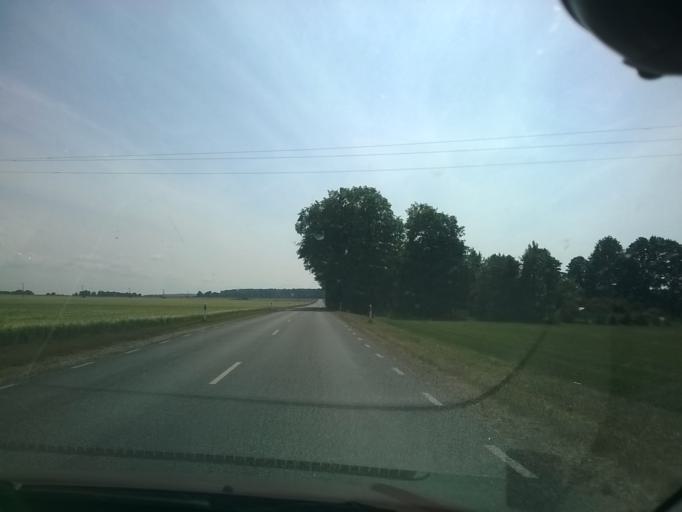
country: EE
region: Tartu
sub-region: Puhja vald
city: Puhja
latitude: 58.2698
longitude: 26.1759
